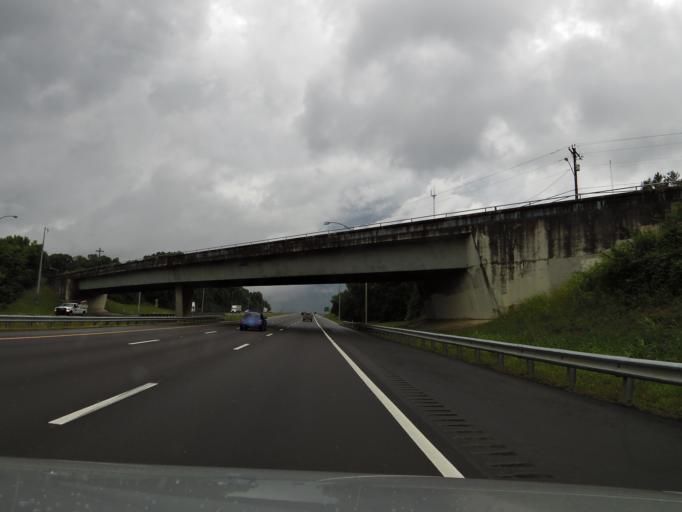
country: US
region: Tennessee
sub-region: Knox County
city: Knoxville
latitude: 35.9869
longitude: -83.9735
